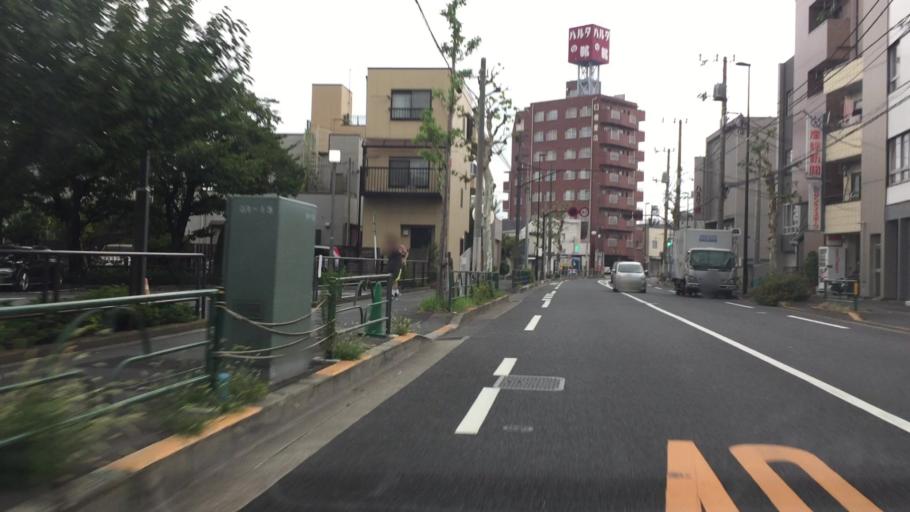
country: JP
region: Saitama
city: Soka
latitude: 35.7455
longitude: 139.7958
